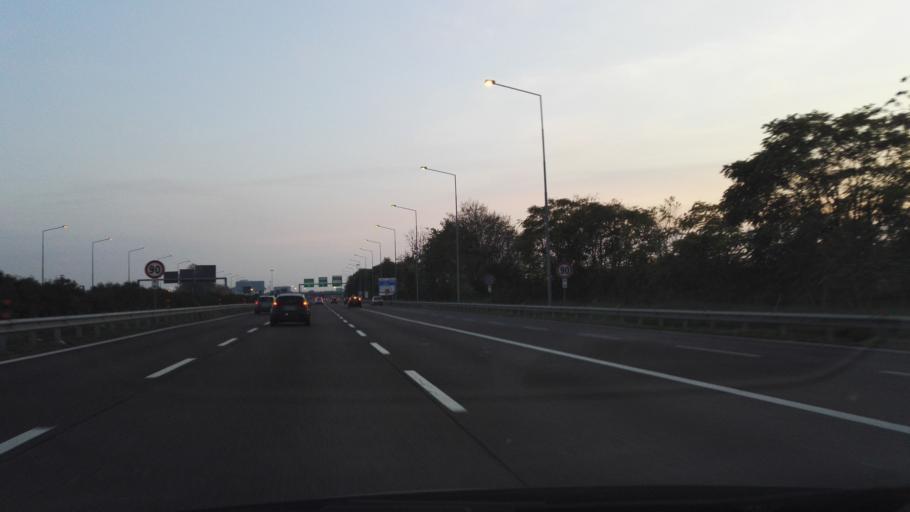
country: IT
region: Lombardy
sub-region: Citta metropolitana di Milano
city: Linate
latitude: 45.4424
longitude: 9.2574
